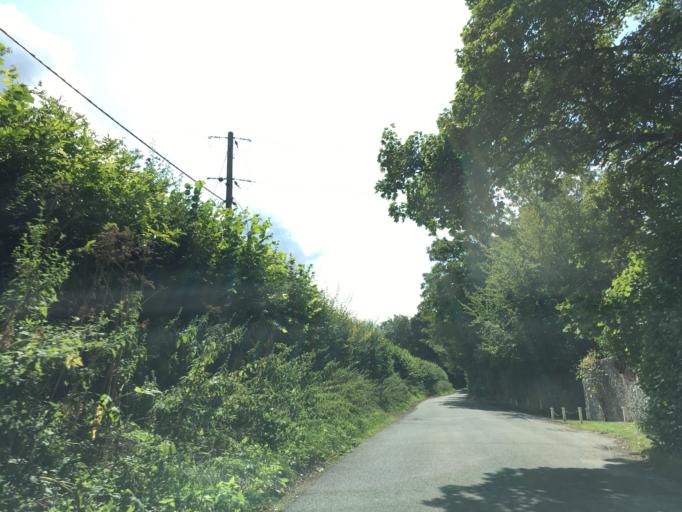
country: GB
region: England
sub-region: Hampshire
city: Colden Common
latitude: 51.0253
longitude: -1.2738
